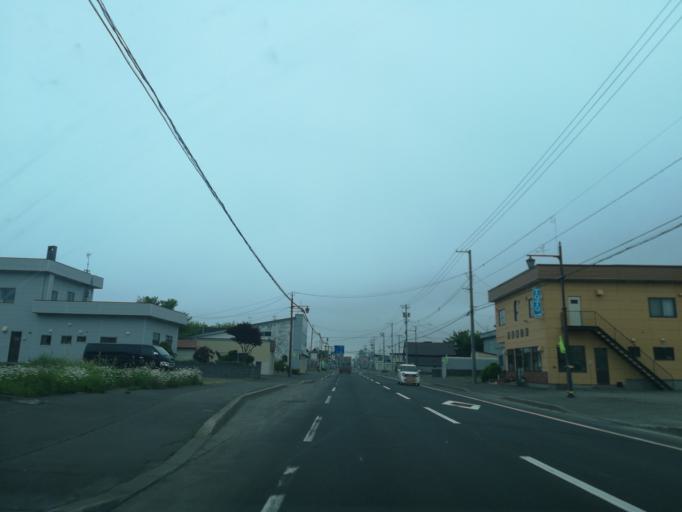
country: JP
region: Hokkaido
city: Ebetsu
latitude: 43.0697
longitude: 141.6495
